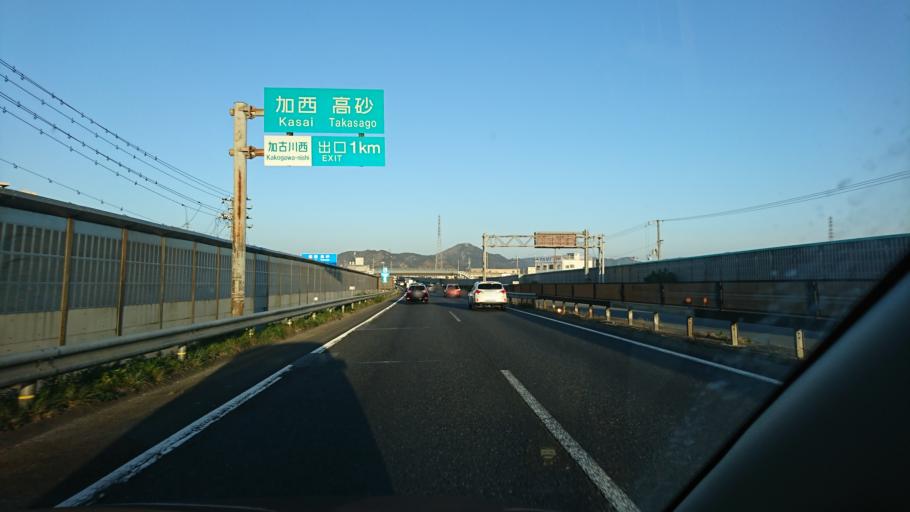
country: JP
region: Hyogo
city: Kakogawacho-honmachi
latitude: 34.7820
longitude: 134.8316
